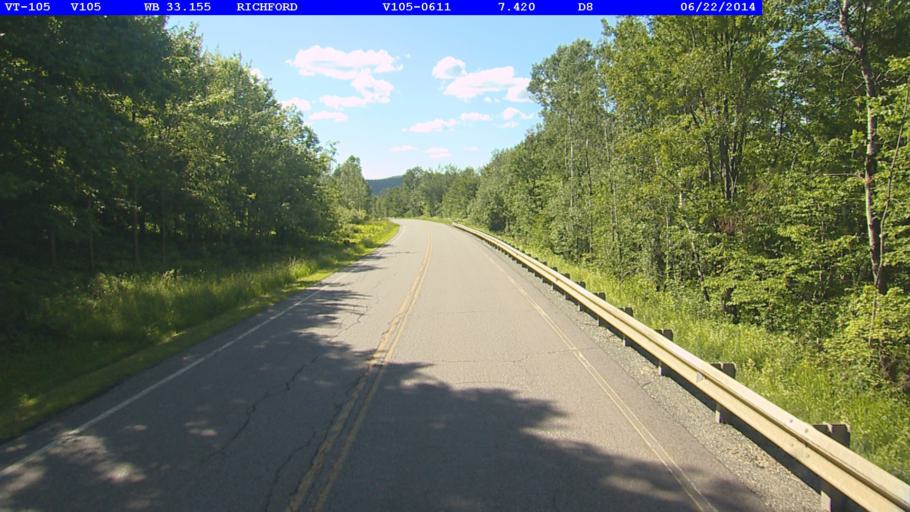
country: US
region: Vermont
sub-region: Franklin County
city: Richford
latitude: 45.0026
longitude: -72.5761
